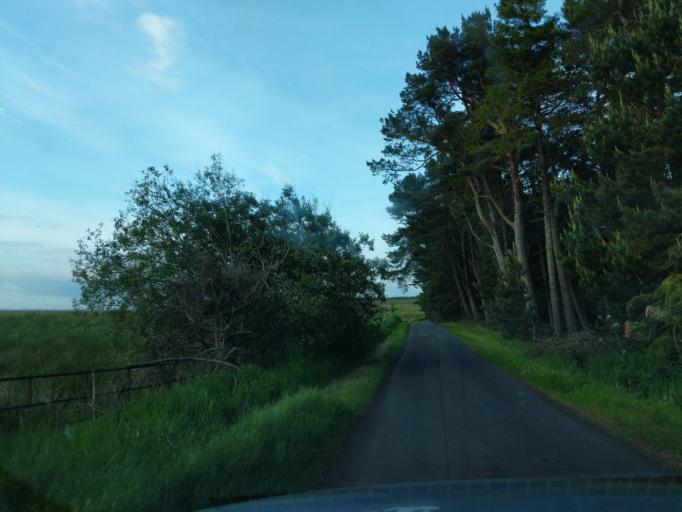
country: GB
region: Scotland
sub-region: Midlothian
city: Gorebridge
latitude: 55.7773
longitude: -3.1078
